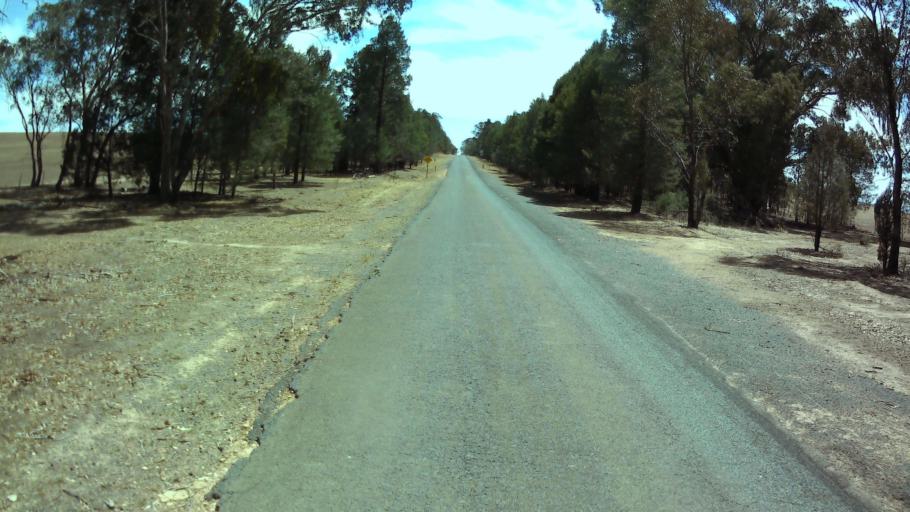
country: AU
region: New South Wales
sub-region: Weddin
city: Grenfell
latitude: -33.7622
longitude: 148.2049
